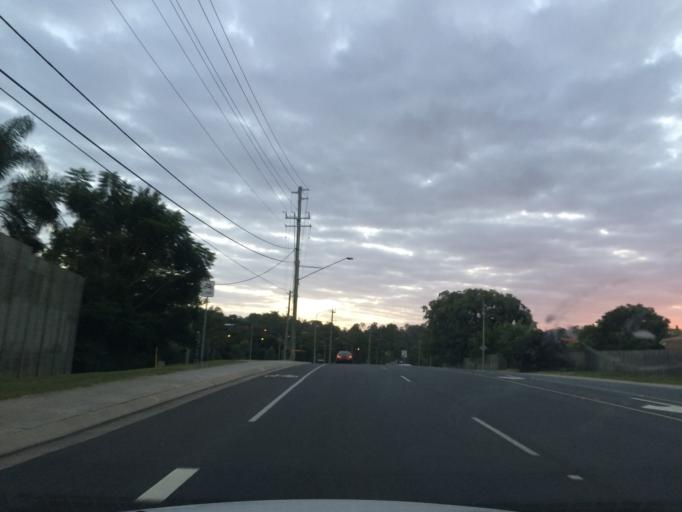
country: AU
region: Queensland
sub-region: Brisbane
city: Kenmore Hills
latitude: -27.5155
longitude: 152.9271
